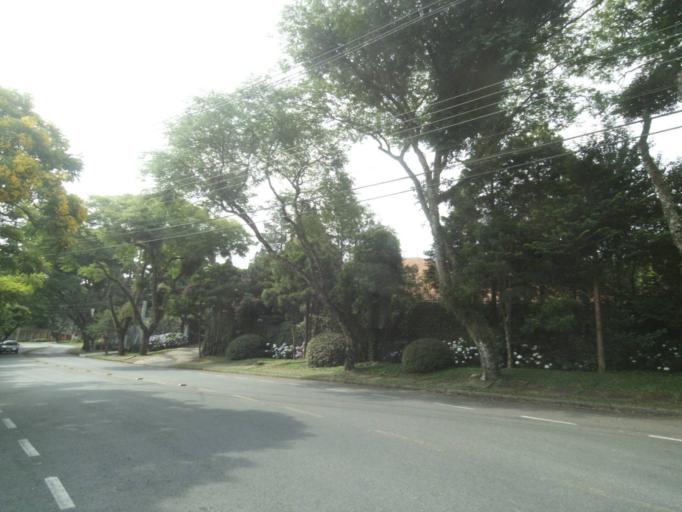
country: BR
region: Parana
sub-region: Curitiba
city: Curitiba
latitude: -25.4052
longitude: -49.2987
